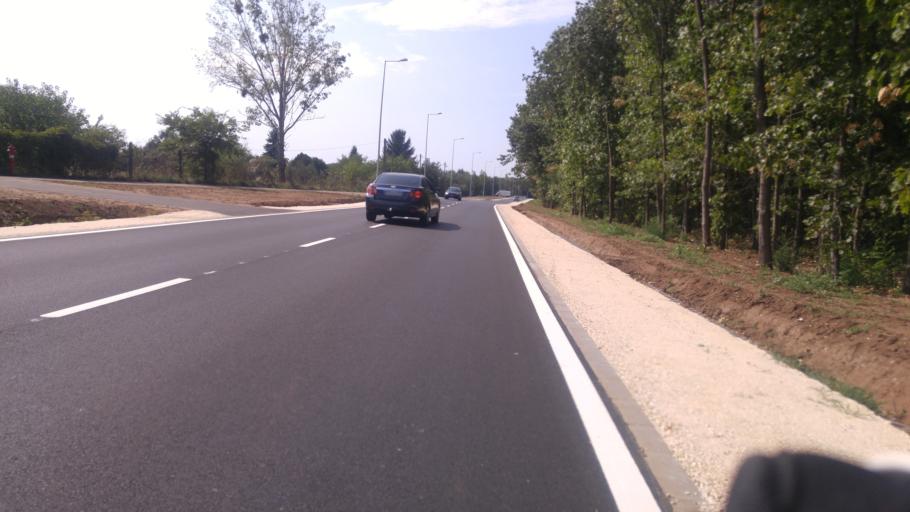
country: HU
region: Budapest
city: Budapest XVII. keruelet
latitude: 47.4502
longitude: 19.2372
